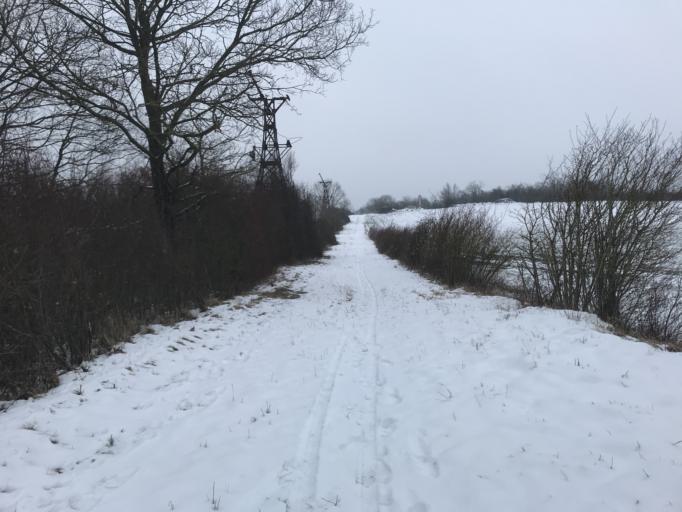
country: LU
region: Luxembourg
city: Belvaux
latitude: 49.5030
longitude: 5.9293
